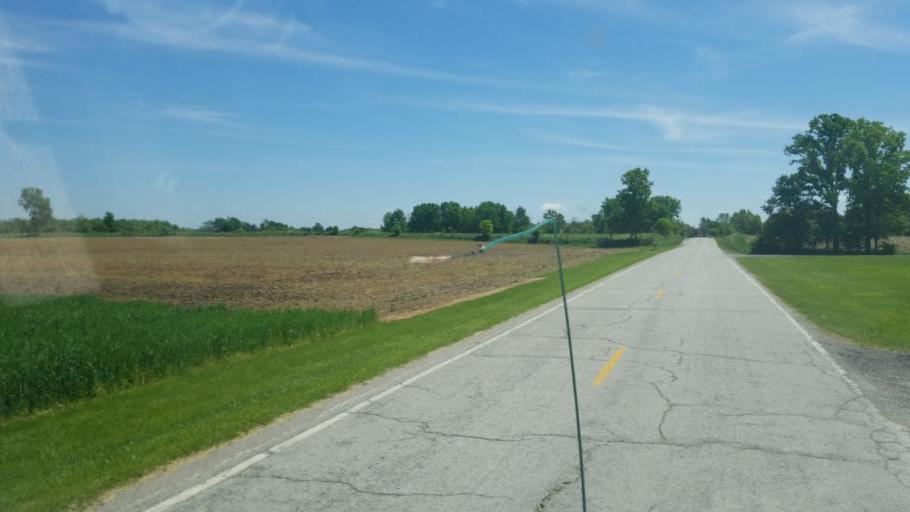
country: US
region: Ohio
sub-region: Huron County
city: Willard
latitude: 41.0887
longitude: -82.7536
